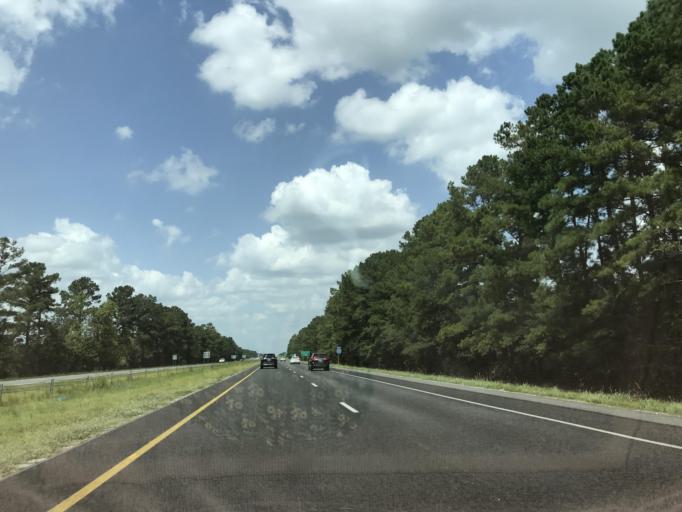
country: US
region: North Carolina
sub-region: Duplin County
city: Wallace
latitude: 34.7610
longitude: -77.9563
